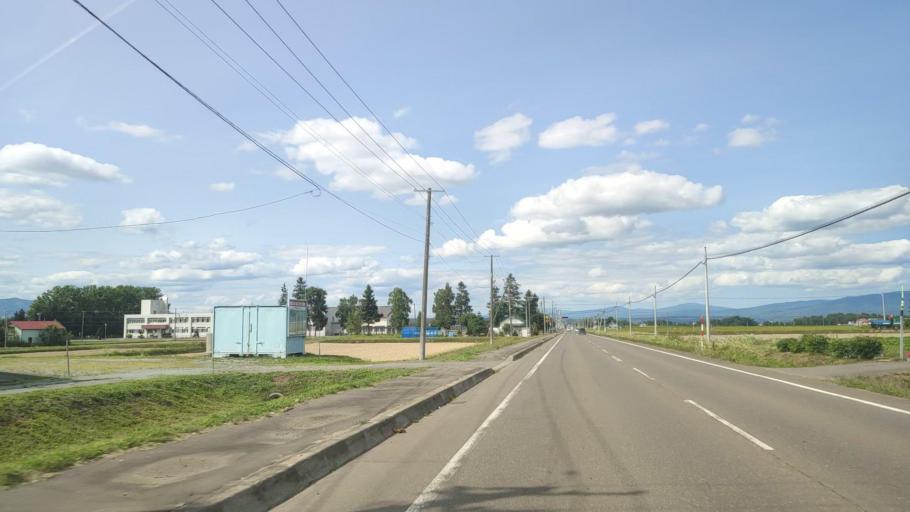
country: JP
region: Hokkaido
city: Nayoro
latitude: 44.2893
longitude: 142.4294
